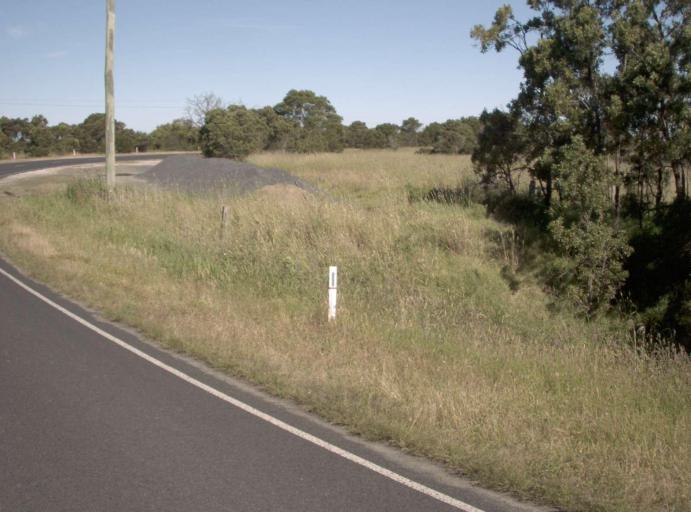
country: AU
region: Victoria
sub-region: Latrobe
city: Traralgon
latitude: -38.6210
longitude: 146.6712
